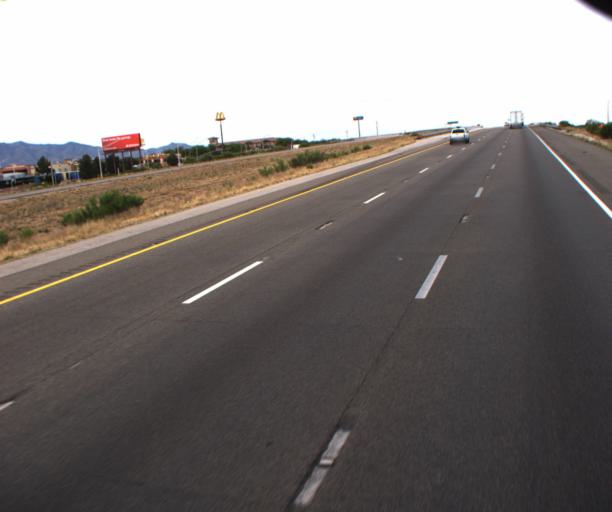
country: US
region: Arizona
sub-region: Cochise County
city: Whetstone
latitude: 31.9654
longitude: -110.3442
